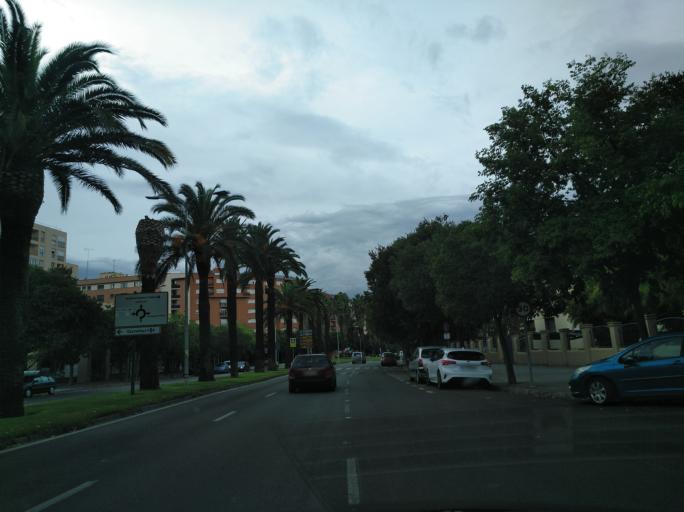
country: ES
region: Extremadura
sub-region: Provincia de Badajoz
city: Badajoz
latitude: 38.8663
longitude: -6.9848
